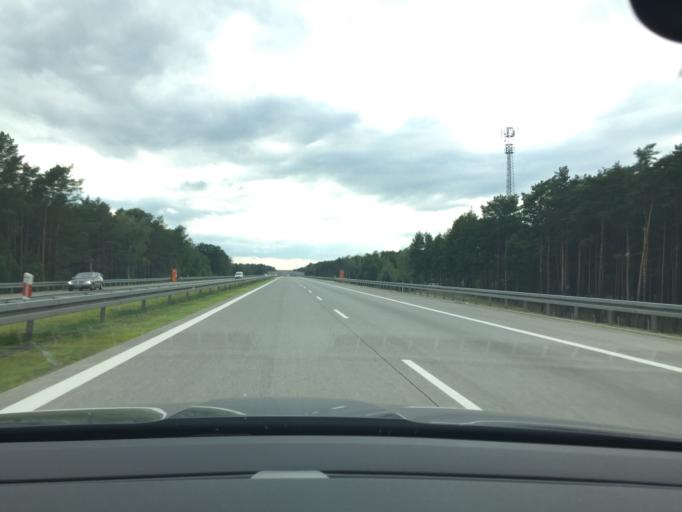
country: PL
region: Lubusz
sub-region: Powiat miedzyrzecki
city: Trzciel
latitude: 52.3297
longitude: 15.9183
